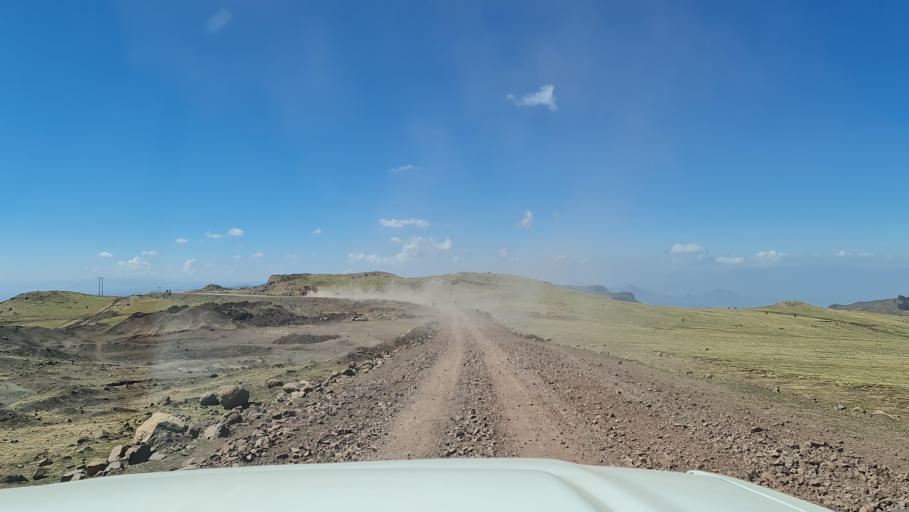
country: ET
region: Amhara
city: Debark'
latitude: 13.2414
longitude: 38.1195
